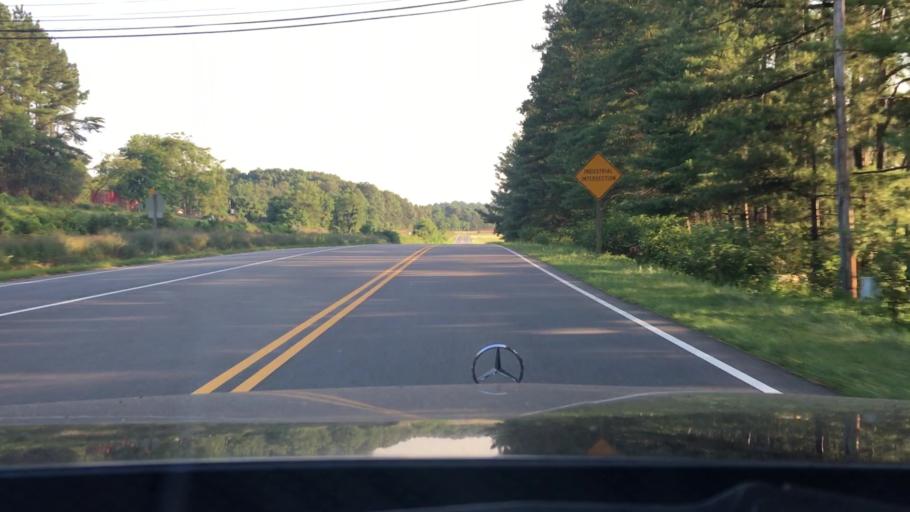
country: US
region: Virginia
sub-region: Pittsylvania County
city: Hurt
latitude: 37.0984
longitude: -79.3052
